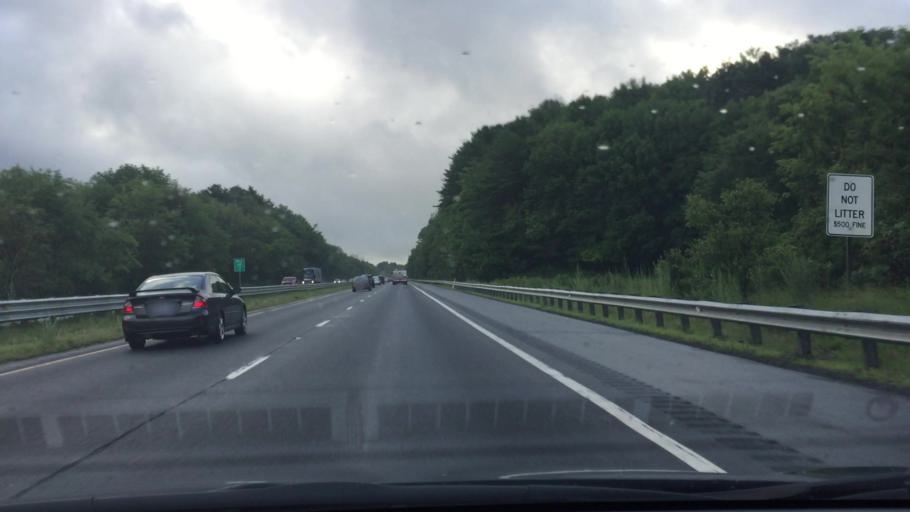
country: US
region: Massachusetts
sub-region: Worcester County
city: Warren
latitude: 42.1802
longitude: -72.2356
